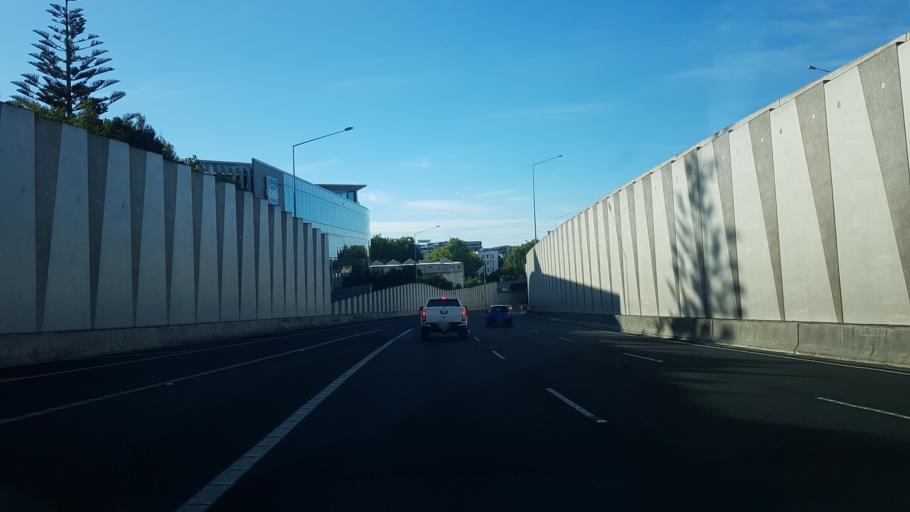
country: NZ
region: Auckland
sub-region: Auckland
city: Auckland
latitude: -36.8513
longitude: 174.7542
